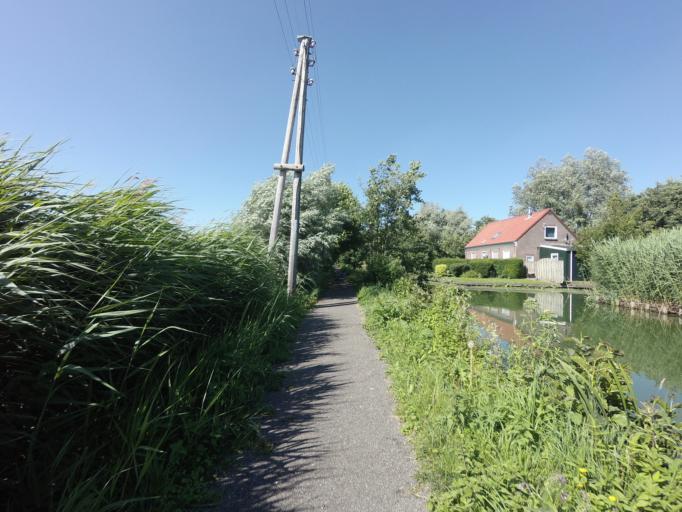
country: NL
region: South Holland
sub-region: Bodegraven-Reeuwijk
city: Reeuwijk
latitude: 52.0397
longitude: 4.7502
